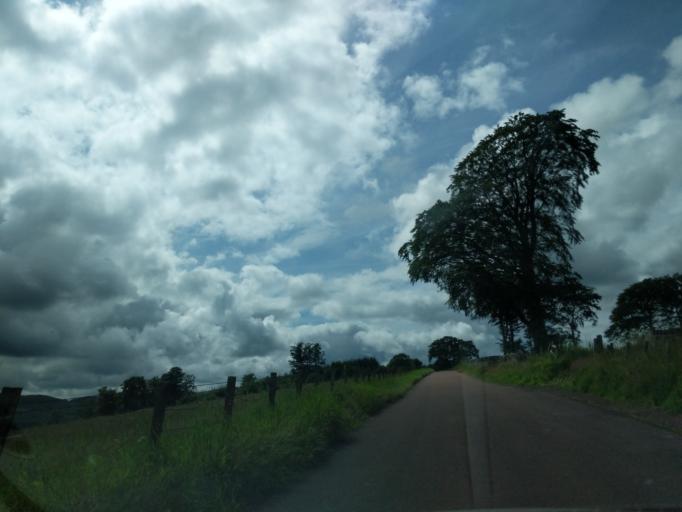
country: GB
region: Scotland
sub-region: South Lanarkshire
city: Carnwath
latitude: 55.6264
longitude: -3.6824
